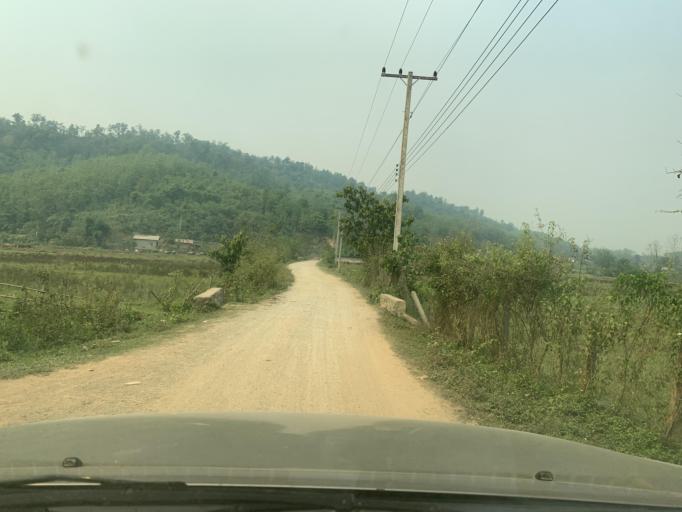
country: LA
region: Louangphabang
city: Louangphabang
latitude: 19.9016
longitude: 102.2544
